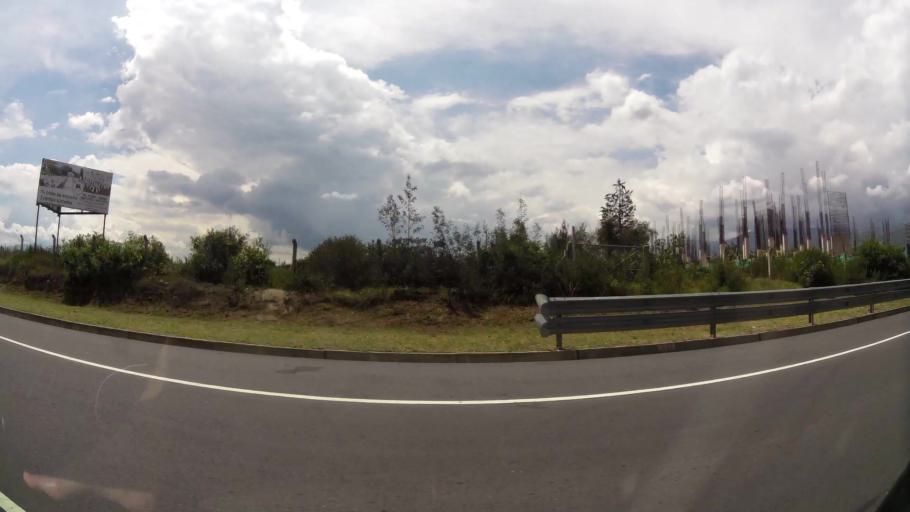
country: EC
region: Pichincha
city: Quito
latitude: -0.1637
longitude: -78.3454
